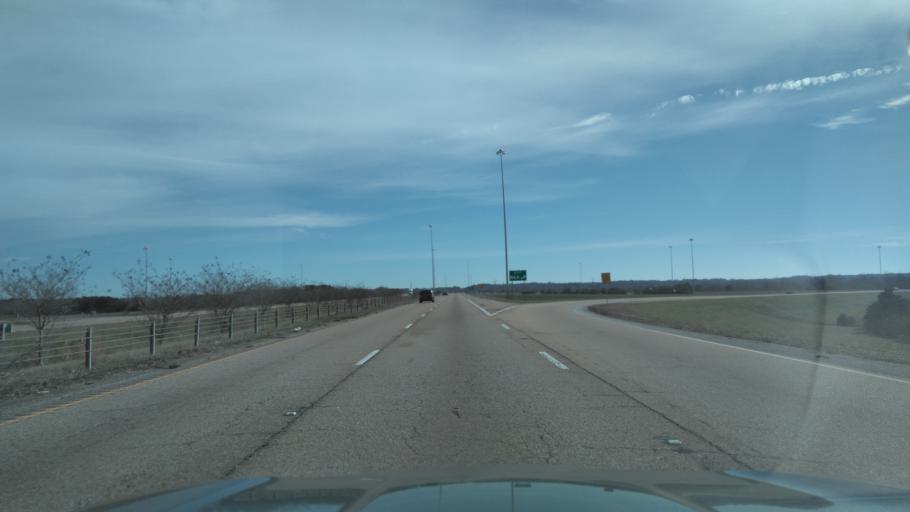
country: US
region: Mississippi
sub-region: Lee County
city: Tupelo
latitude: 34.2963
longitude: -88.7075
